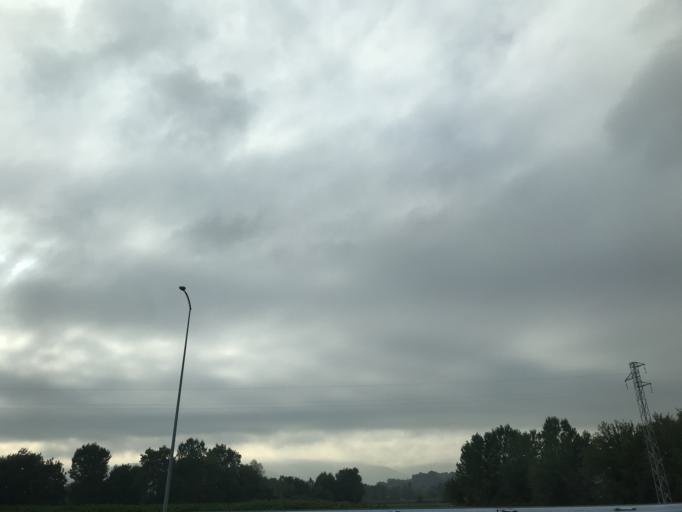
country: TR
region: Balikesir
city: Susurluk
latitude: 39.9257
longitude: 28.1344
